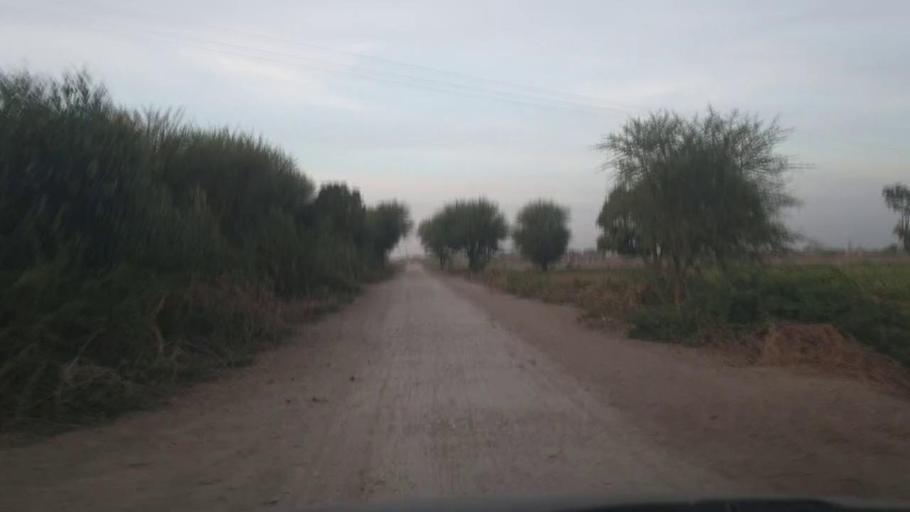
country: PK
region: Sindh
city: Kunri
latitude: 25.2333
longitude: 69.5202
